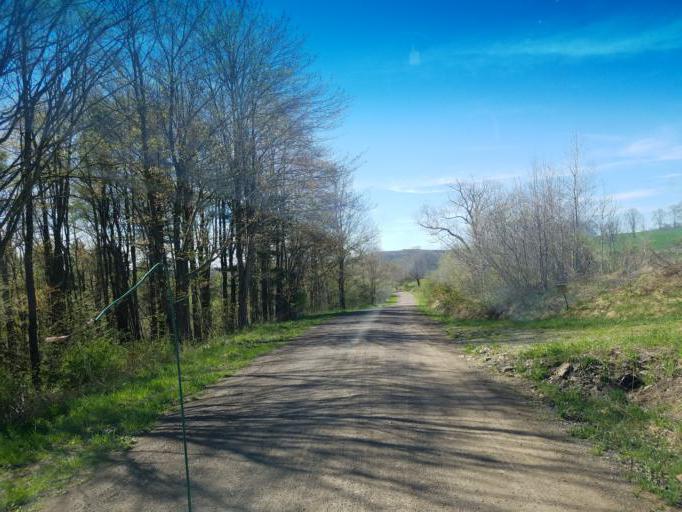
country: US
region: New York
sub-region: Allegany County
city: Andover
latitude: 41.9626
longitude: -77.7816
